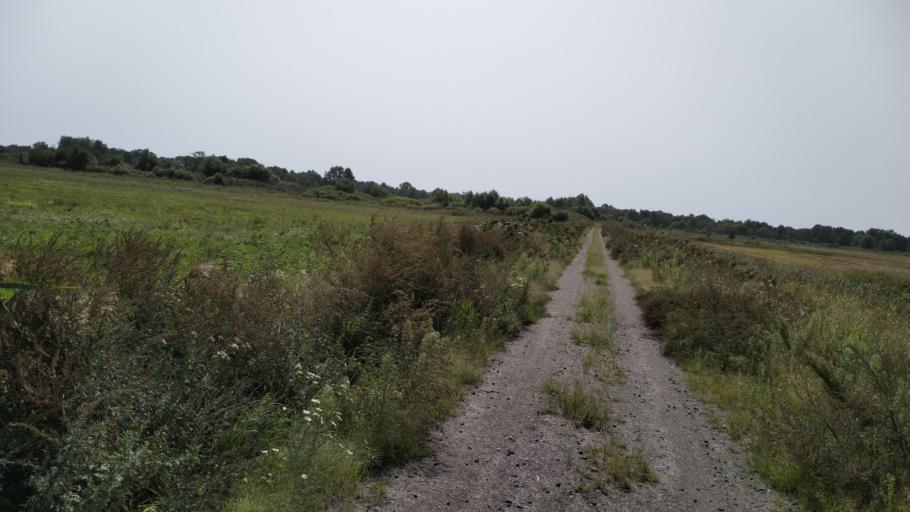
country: BY
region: Brest
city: Davyd-Haradok
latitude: 51.9703
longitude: 27.1738
